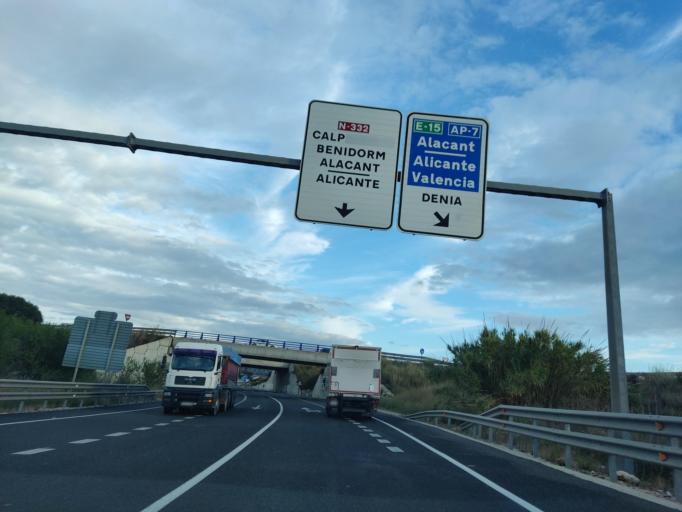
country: ES
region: Valencia
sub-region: Provincia de Alicante
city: Ondara
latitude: 38.8198
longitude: 0.0187
